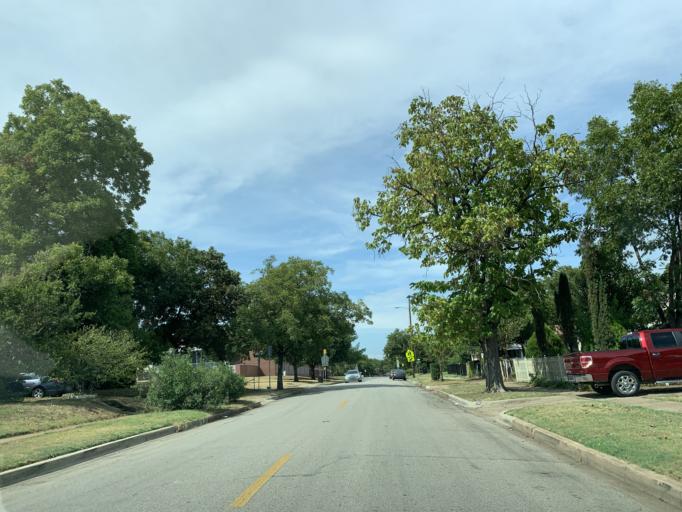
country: US
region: Texas
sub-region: Dallas County
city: Cockrell Hill
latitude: 32.7382
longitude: -96.8442
